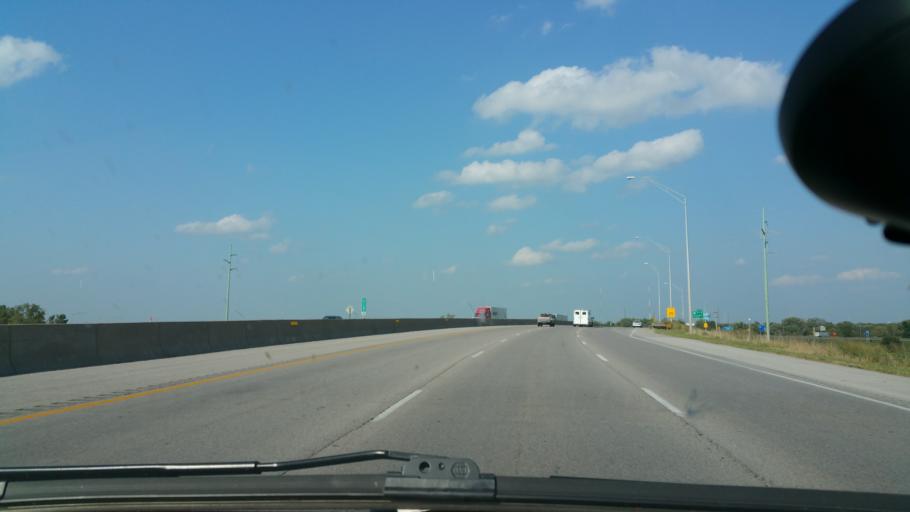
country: US
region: Iowa
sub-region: Polk County
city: Grimes
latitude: 41.6476
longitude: -93.7753
